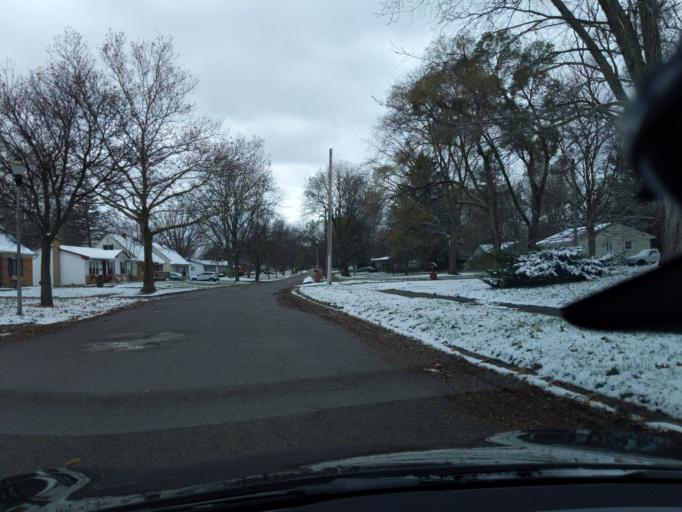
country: US
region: Michigan
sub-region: Eaton County
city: Waverly
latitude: 42.6863
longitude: -84.5968
